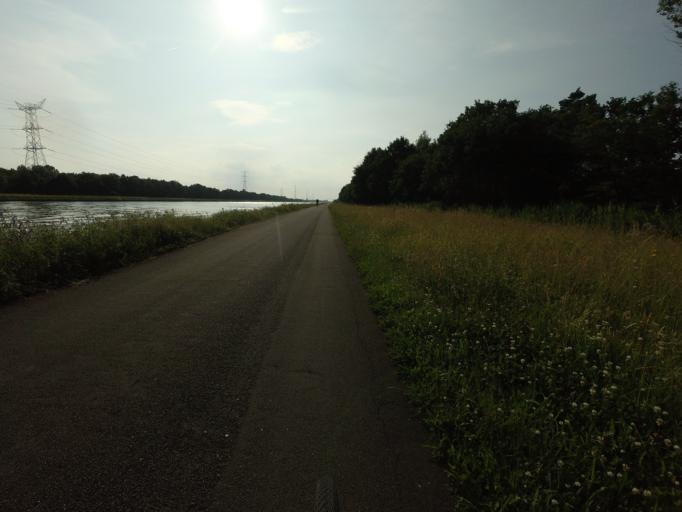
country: BE
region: Flanders
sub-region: Provincie Antwerpen
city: Nijlen
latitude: 51.1869
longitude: 4.6890
